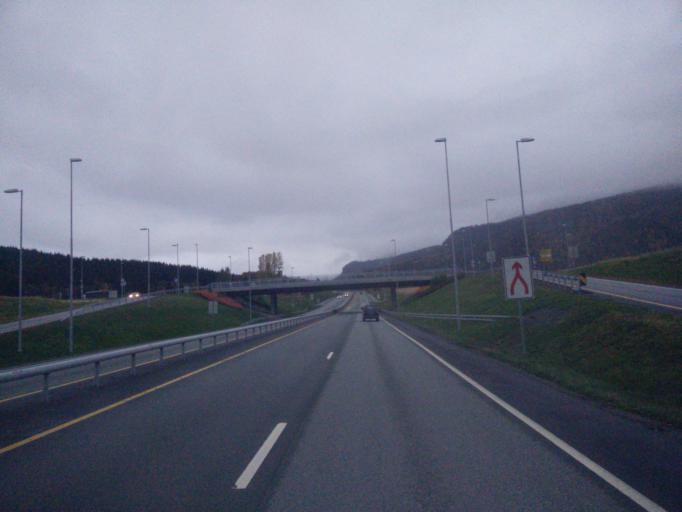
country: NO
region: Nord-Trondelag
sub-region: Stjordal
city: Stjordal
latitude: 63.4891
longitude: 10.8855
